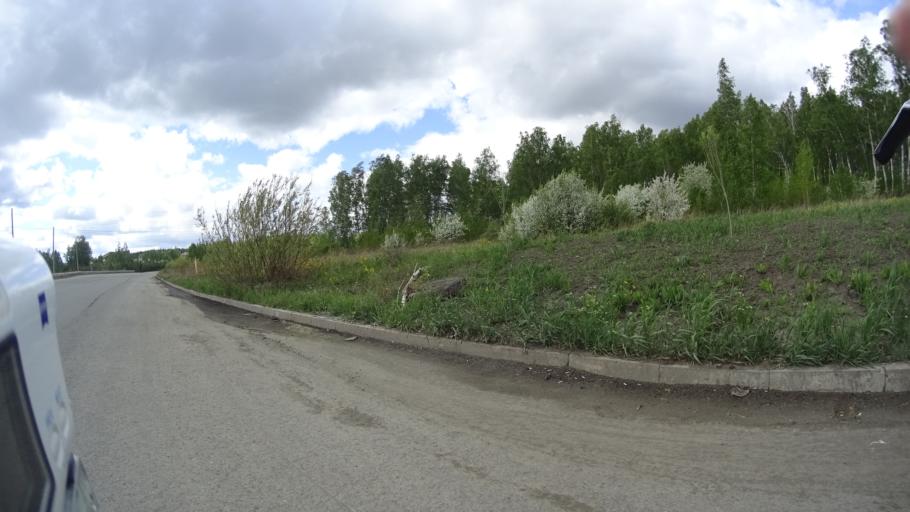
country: RU
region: Chelyabinsk
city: Sargazy
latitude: 55.1531
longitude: 61.2675
